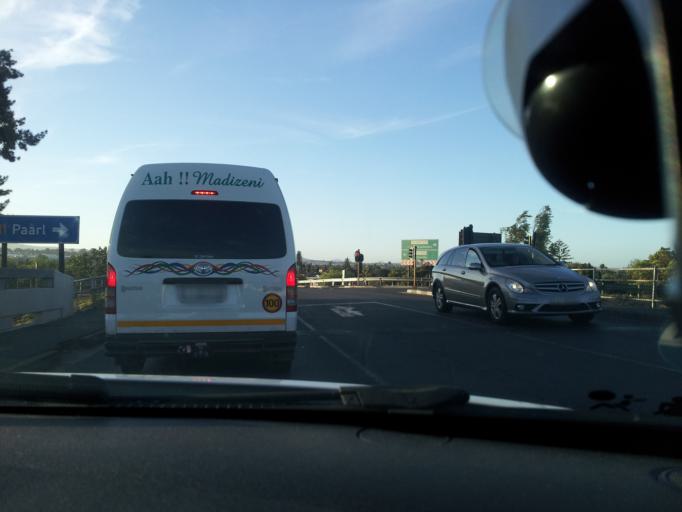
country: ZA
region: Western Cape
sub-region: City of Cape Town
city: Kraaifontein
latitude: -33.8451
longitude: 18.7150
